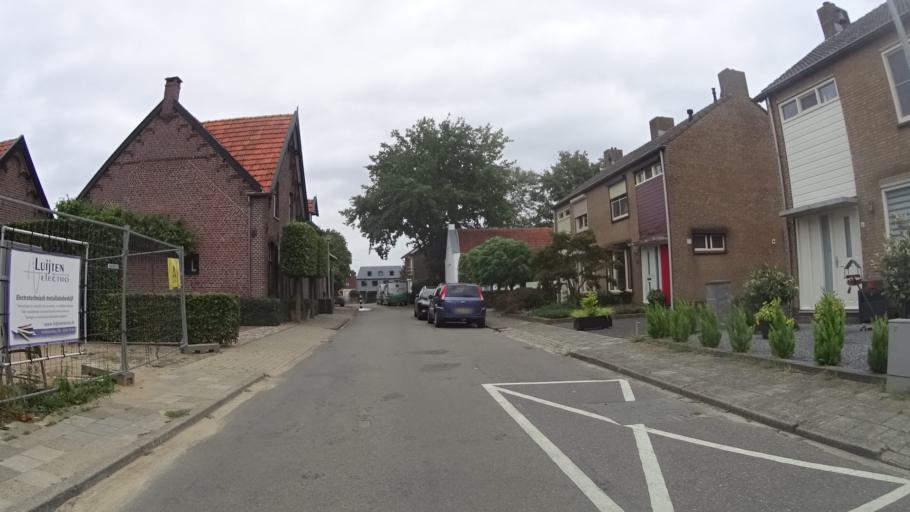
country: NL
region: Limburg
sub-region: Gemeente Leudal
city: Haelen
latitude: 51.2338
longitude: 5.9768
